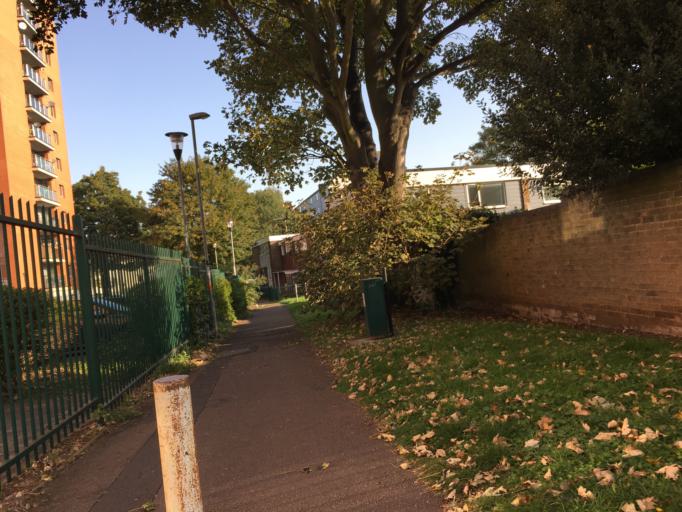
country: GB
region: England
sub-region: Northamptonshire
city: Northampton
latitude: 52.2400
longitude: -0.9017
